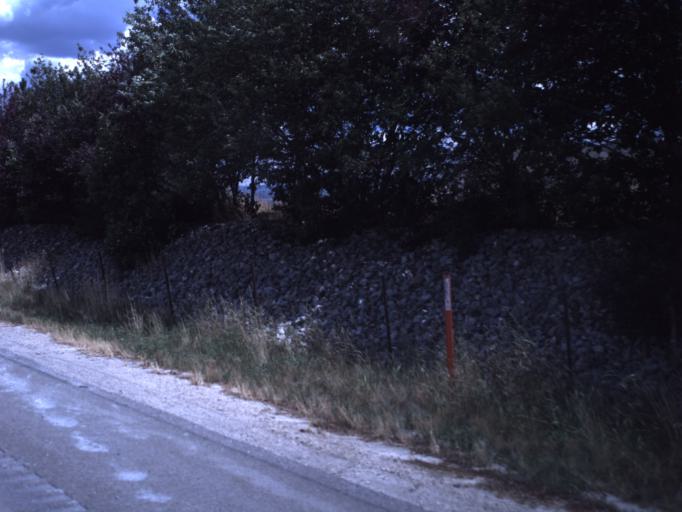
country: US
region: Utah
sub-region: Wasatch County
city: Midway
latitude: 40.4666
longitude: -111.4550
